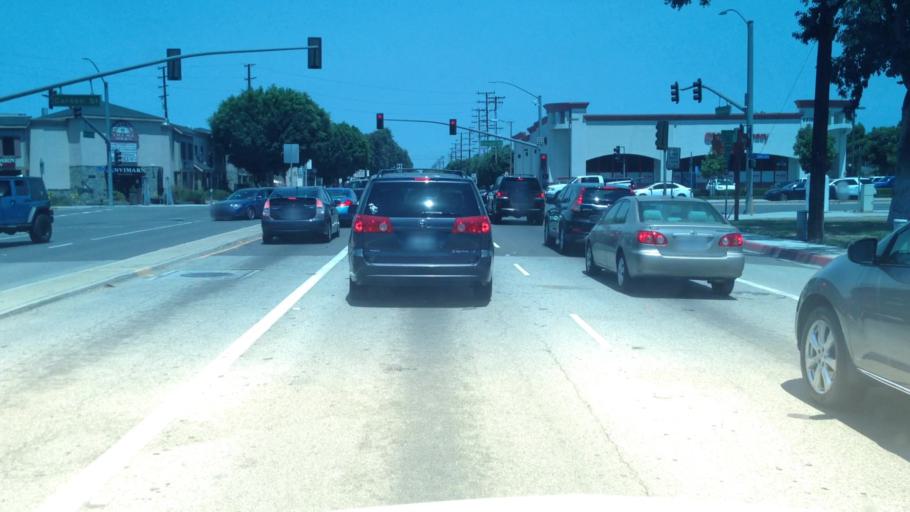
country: US
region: California
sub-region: Los Angeles County
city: Lakewood
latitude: 33.8318
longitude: -118.1251
